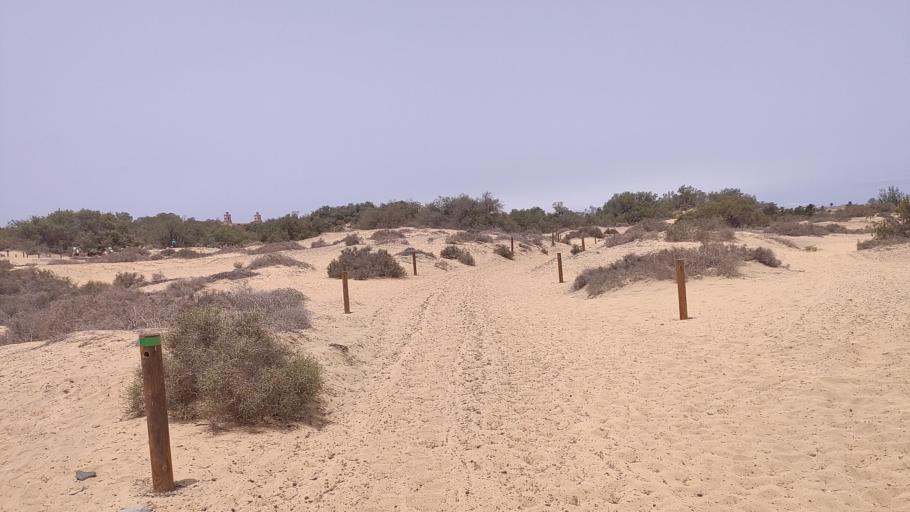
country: ES
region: Canary Islands
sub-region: Provincia de Las Palmas
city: Maspalomas
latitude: 27.7453
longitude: -15.5918
